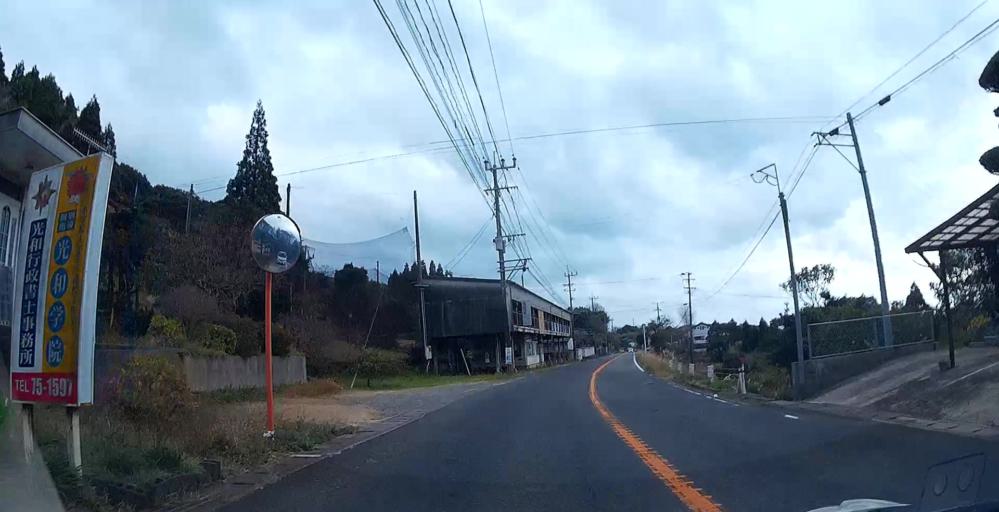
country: JP
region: Kagoshima
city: Akune
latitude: 32.0978
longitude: 130.1770
